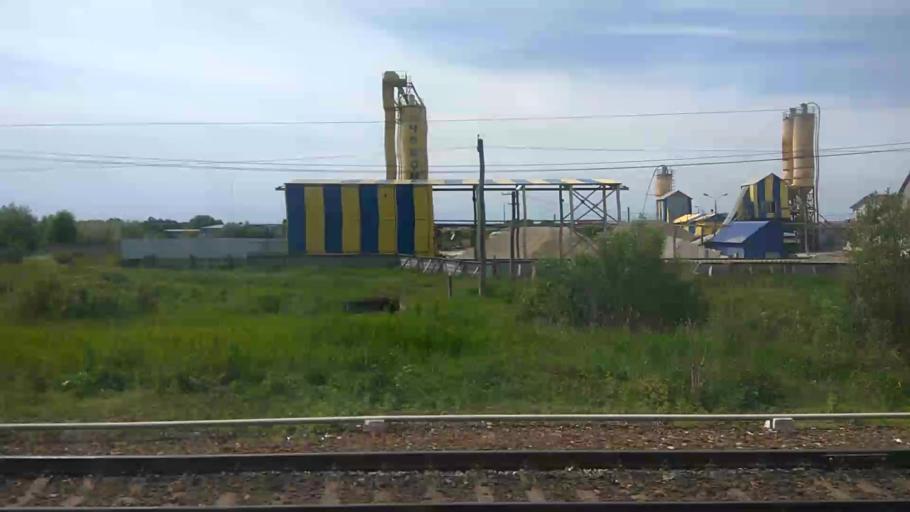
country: RU
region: Moskovskaya
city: Malyshevo
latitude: 55.5046
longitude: 38.3532
